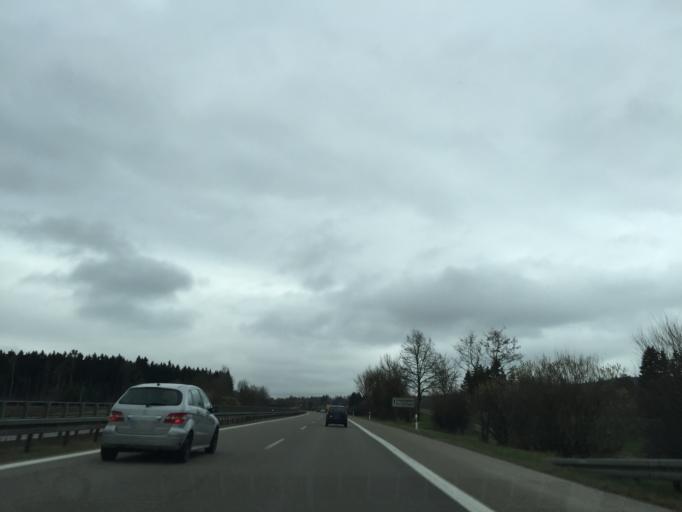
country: DE
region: Baden-Wuerttemberg
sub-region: Freiburg Region
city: Bad Durrheim
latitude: 48.0022
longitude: 8.5317
